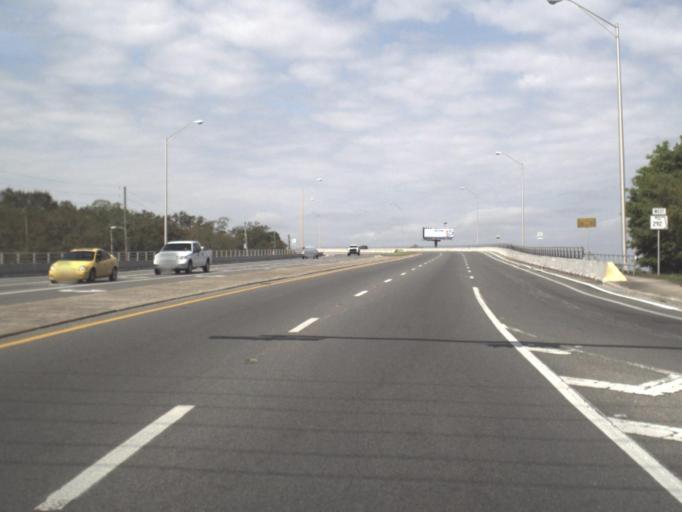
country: US
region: Florida
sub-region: Escambia County
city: Pensacola
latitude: 30.4037
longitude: -87.2424
